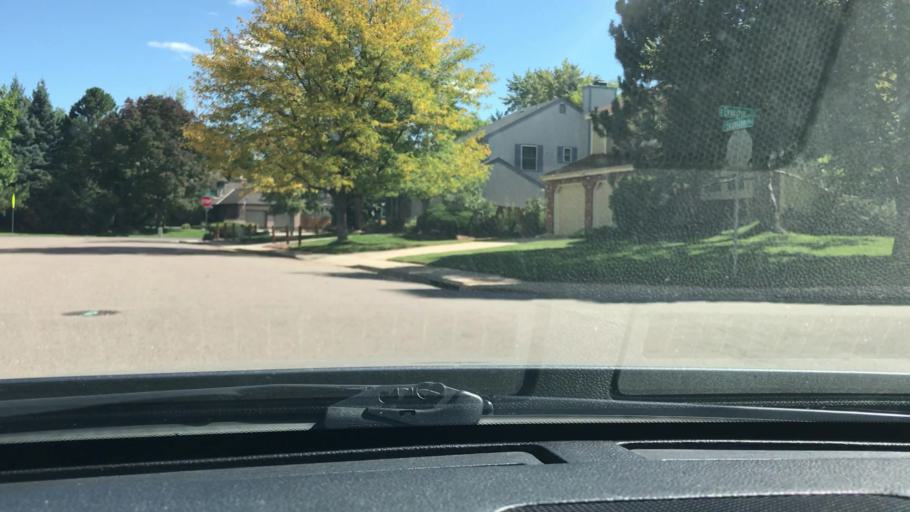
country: US
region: Colorado
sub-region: Arapahoe County
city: Dove Valley
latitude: 39.6285
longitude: -104.8141
